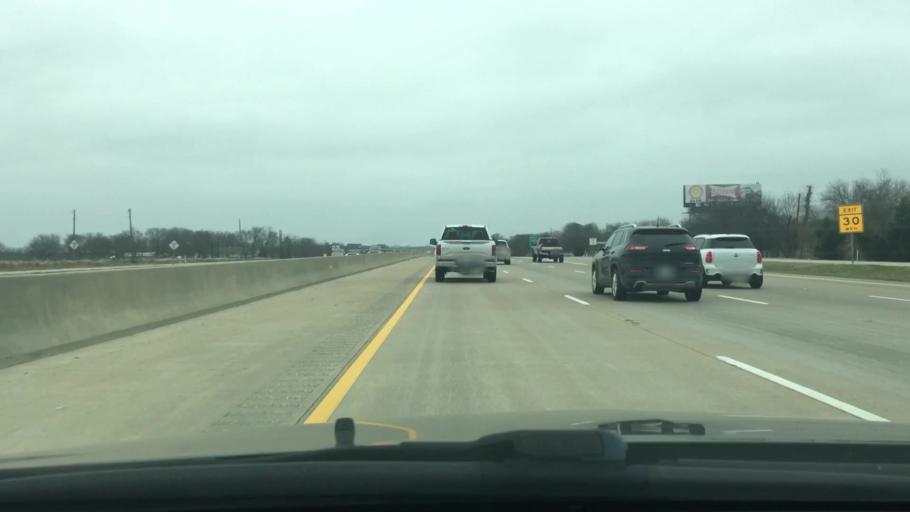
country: US
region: Texas
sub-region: Ellis County
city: Ennis
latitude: 32.2522
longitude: -96.5010
